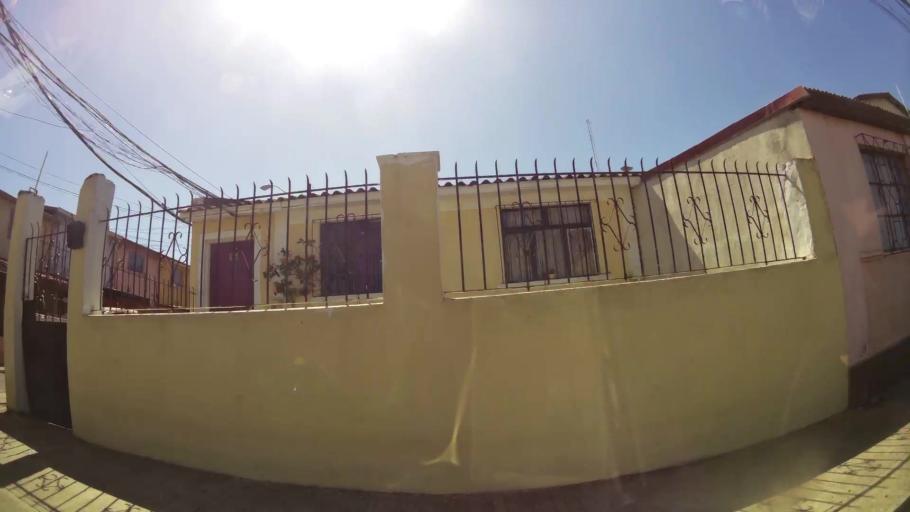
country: CL
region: Valparaiso
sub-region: Provincia de Valparaiso
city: Valparaiso
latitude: -33.0497
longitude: -71.6487
